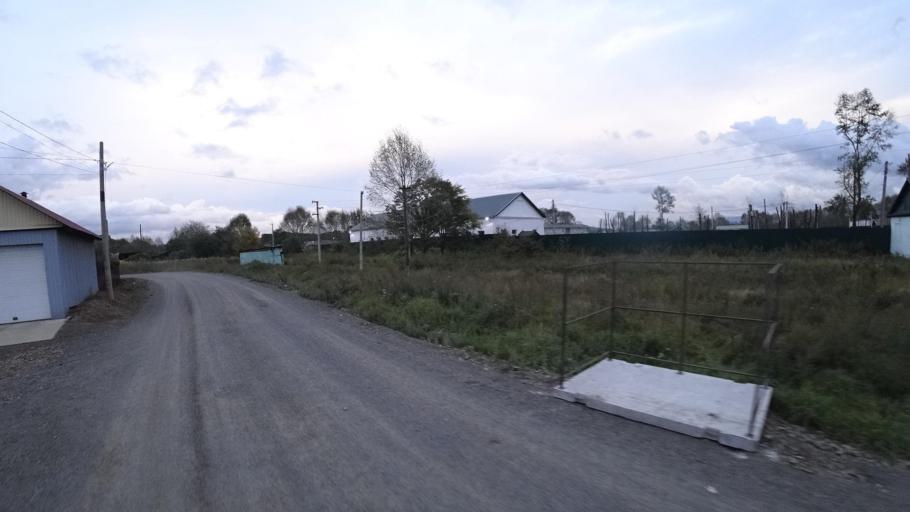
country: RU
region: Jewish Autonomous Oblast
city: Izvestkovyy
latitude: 48.9883
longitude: 131.5528
